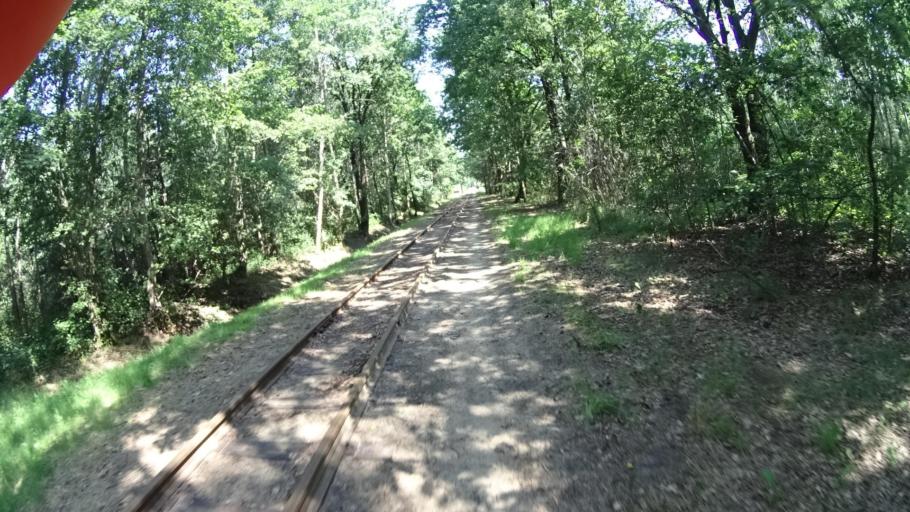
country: PL
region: Masovian Voivodeship
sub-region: Powiat piaseczynski
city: Tarczyn
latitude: 51.9902
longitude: 20.8881
